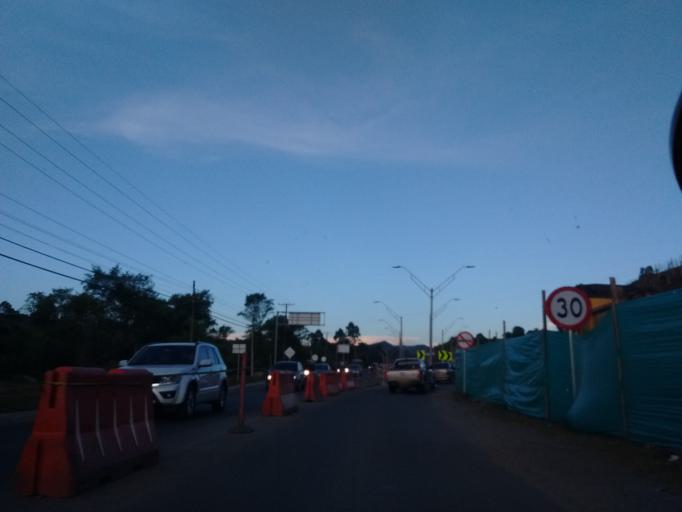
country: CO
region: Antioquia
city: Marinilla
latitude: 6.1686
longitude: -75.3293
